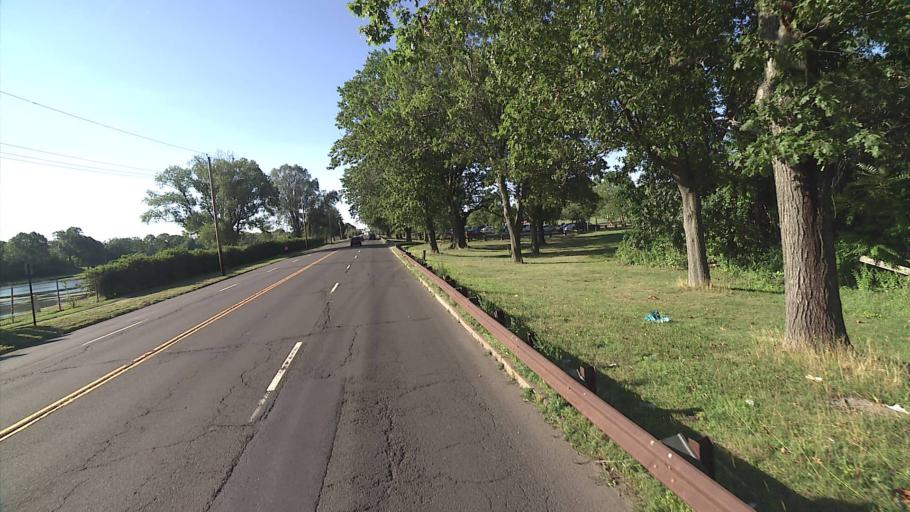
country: US
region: Connecticut
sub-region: New Haven County
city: New Haven
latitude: 41.3022
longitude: -72.9512
